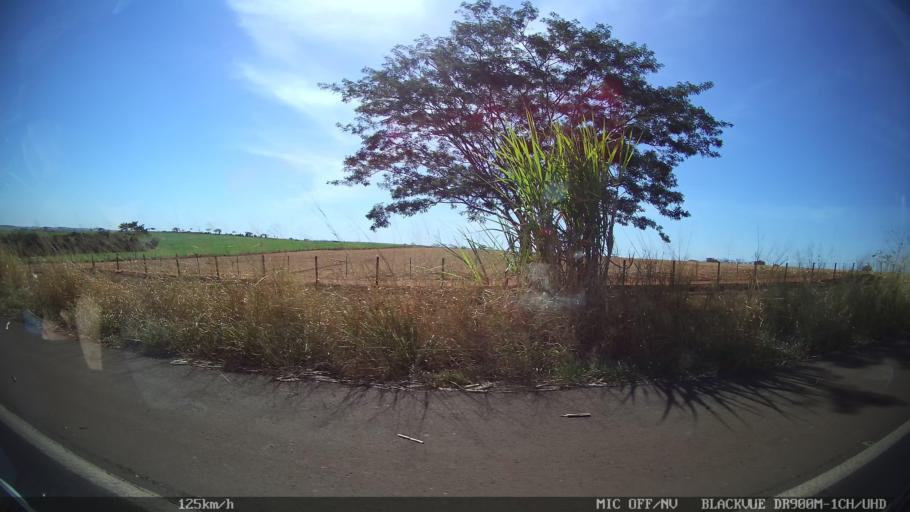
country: BR
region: Sao Paulo
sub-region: Olimpia
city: Olimpia
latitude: -20.6258
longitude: -48.7871
